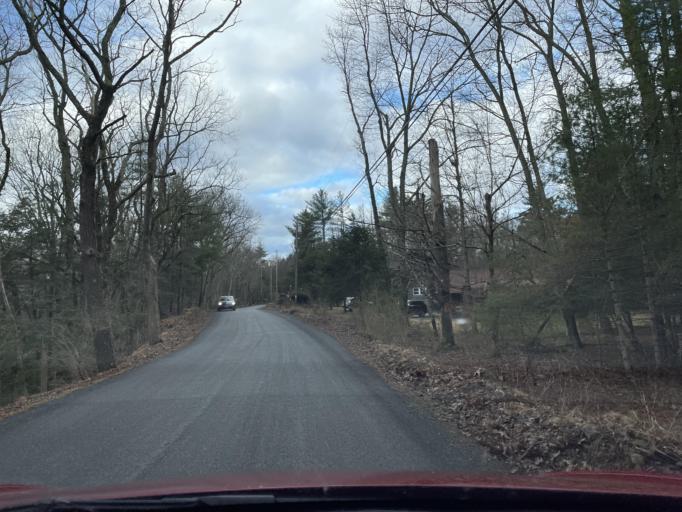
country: US
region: New York
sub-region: Ulster County
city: Manorville
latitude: 42.0816
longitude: -74.0480
